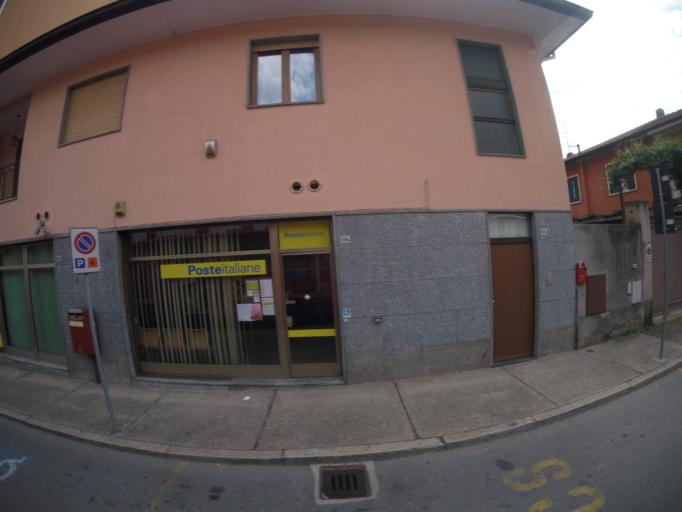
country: IT
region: Piedmont
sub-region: Provincia Verbano-Cusio-Ossola
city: Omegna
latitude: 45.8938
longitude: 8.4115
